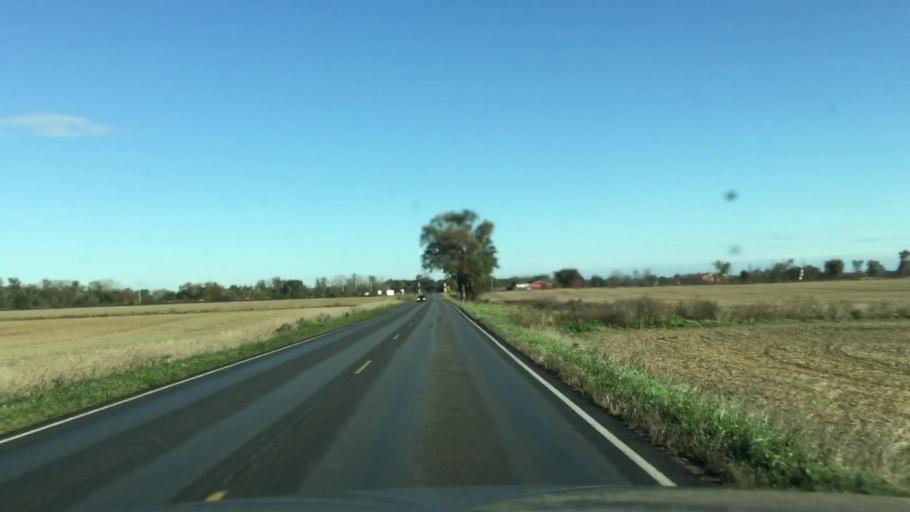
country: US
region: Michigan
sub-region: Shiawassee County
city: Durand
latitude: 42.9150
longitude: -83.9484
